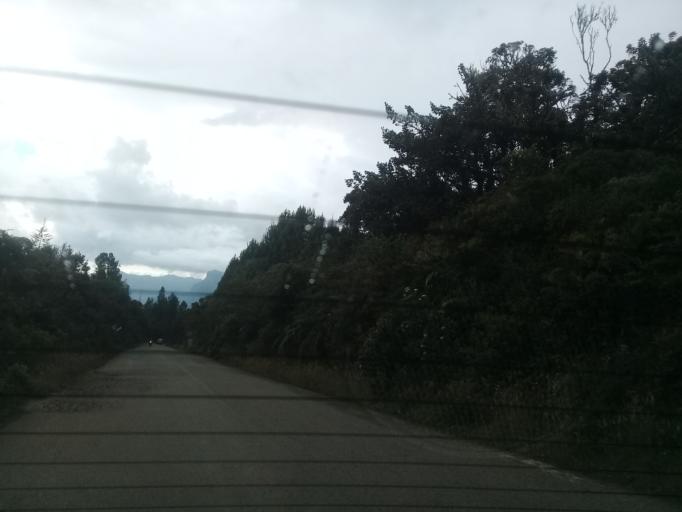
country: CO
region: Cundinamarca
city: Junin
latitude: 4.8489
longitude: -73.7436
